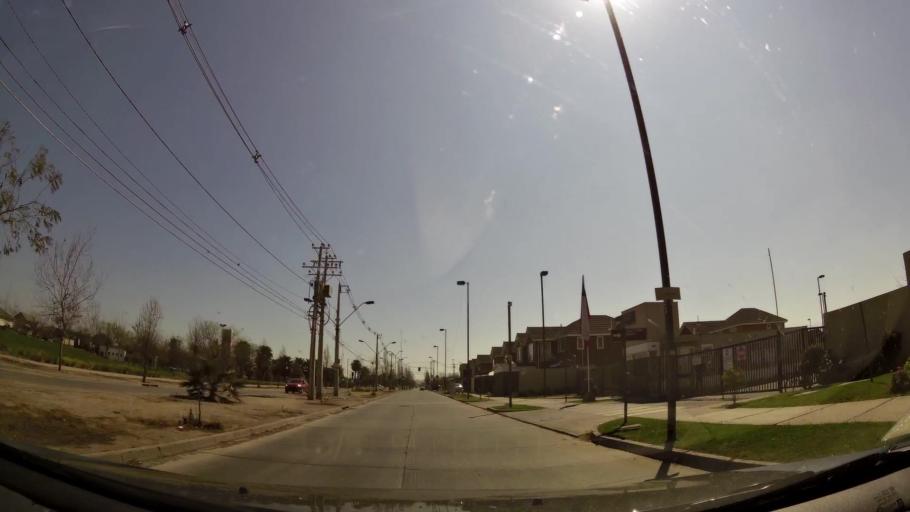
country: CL
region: Santiago Metropolitan
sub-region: Provincia de Chacabuco
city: Chicureo Abajo
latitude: -33.3257
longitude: -70.7464
